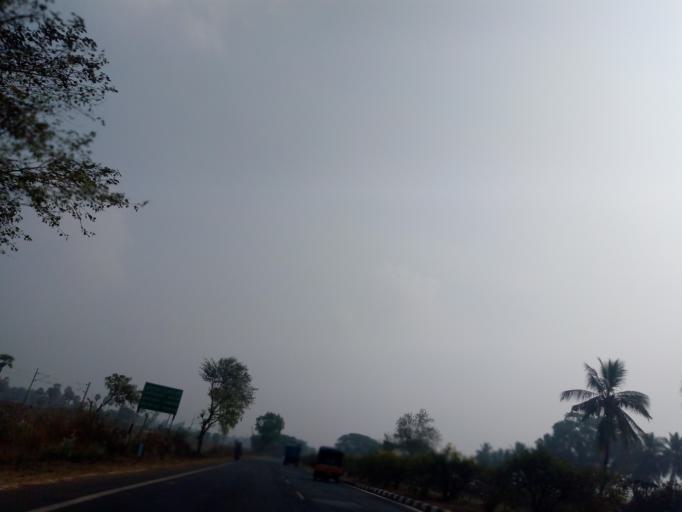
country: IN
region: Andhra Pradesh
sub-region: West Godavari
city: Tadepallegudem
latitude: 16.8168
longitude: 81.3848
